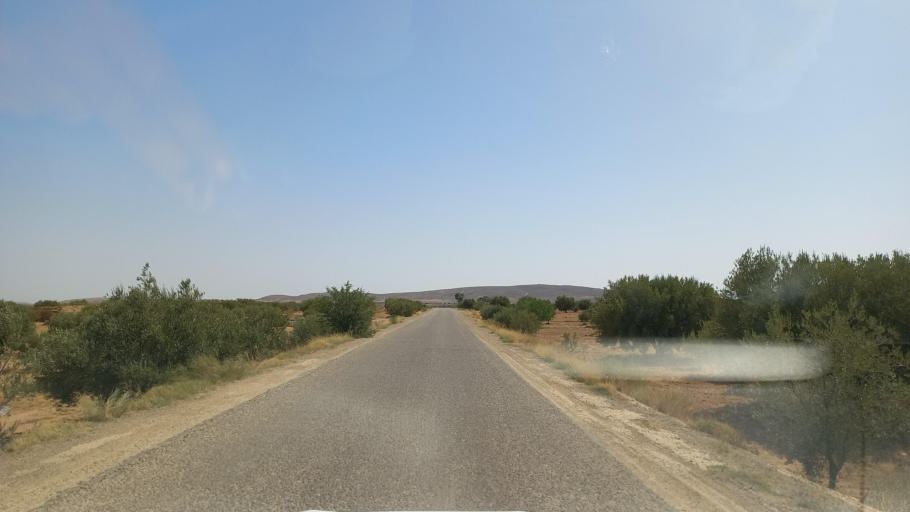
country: TN
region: Al Qasrayn
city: Kasserine
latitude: 35.2145
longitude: 9.0418
